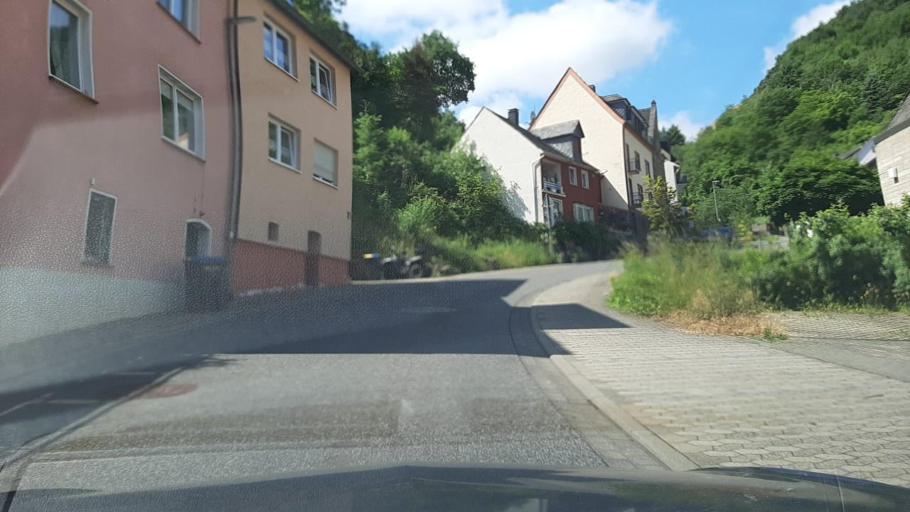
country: DE
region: Rheinland-Pfalz
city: Cochem
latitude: 50.1368
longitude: 7.1784
